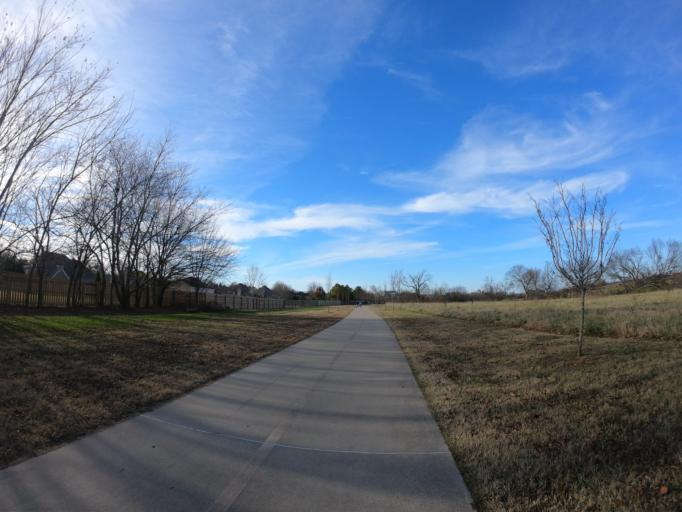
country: US
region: Arkansas
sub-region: Benton County
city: Lowell
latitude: 36.2922
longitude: -94.1733
